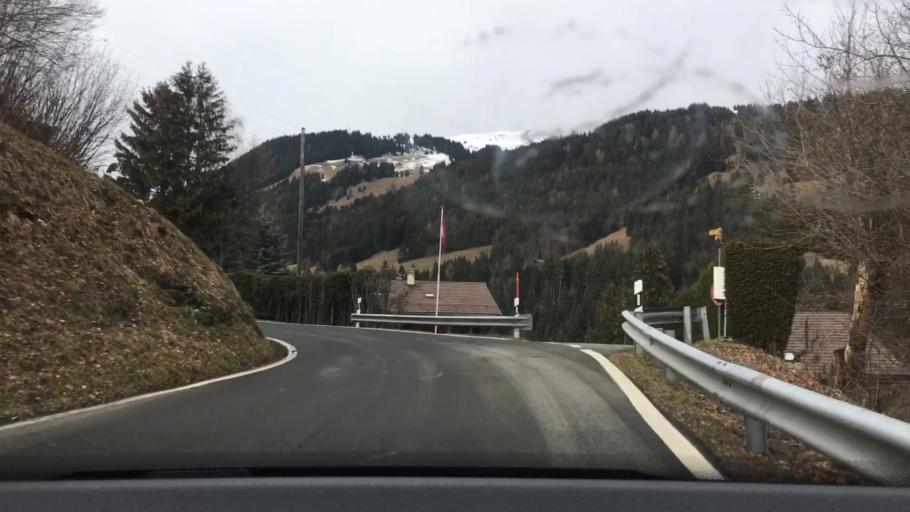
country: CH
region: Valais
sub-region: Monthey District
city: Troistorrents
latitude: 46.2318
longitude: 6.9043
